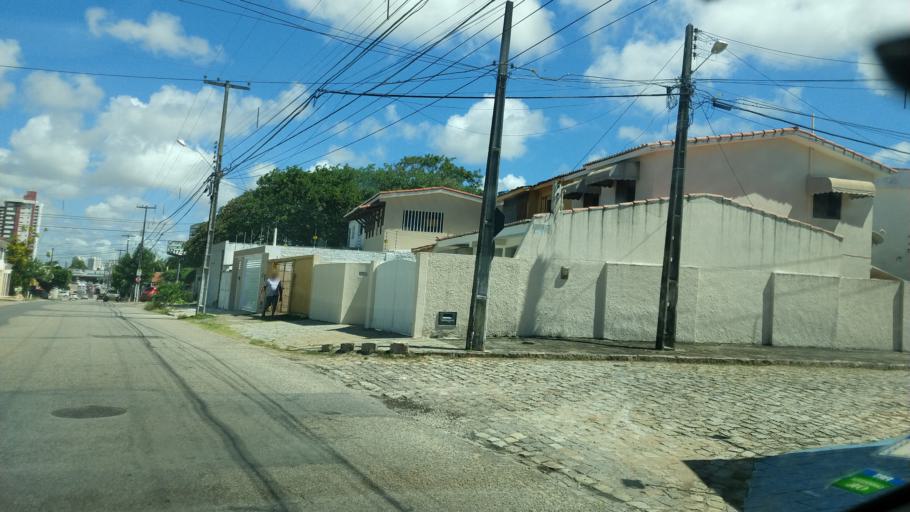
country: BR
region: Rio Grande do Norte
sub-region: Natal
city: Natal
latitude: -5.8500
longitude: -35.2008
